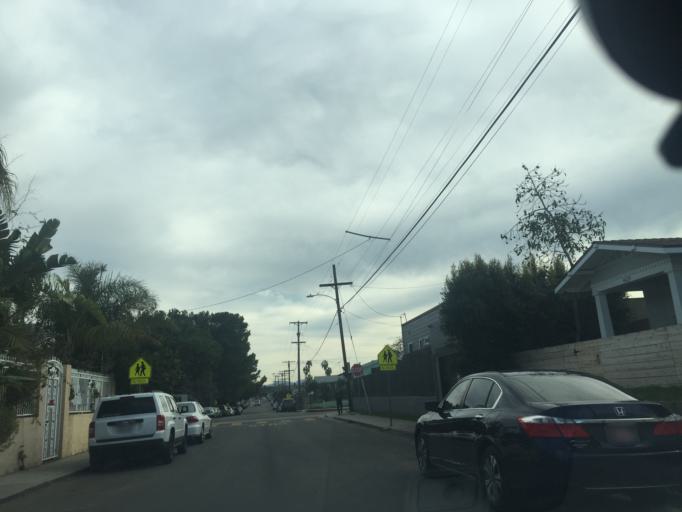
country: US
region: California
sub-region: San Diego County
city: Lemon Grove
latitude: 32.7514
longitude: -117.0950
